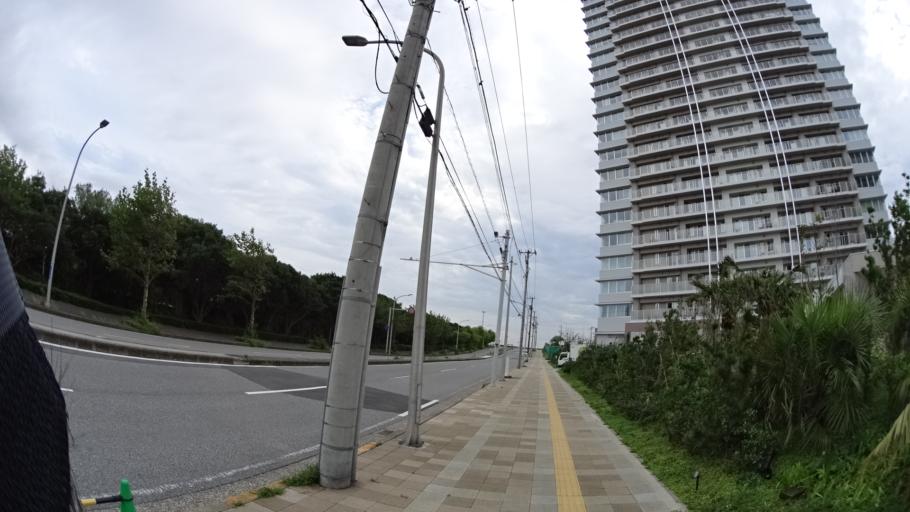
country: JP
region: Chiba
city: Chiba
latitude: 35.6348
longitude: 140.0448
